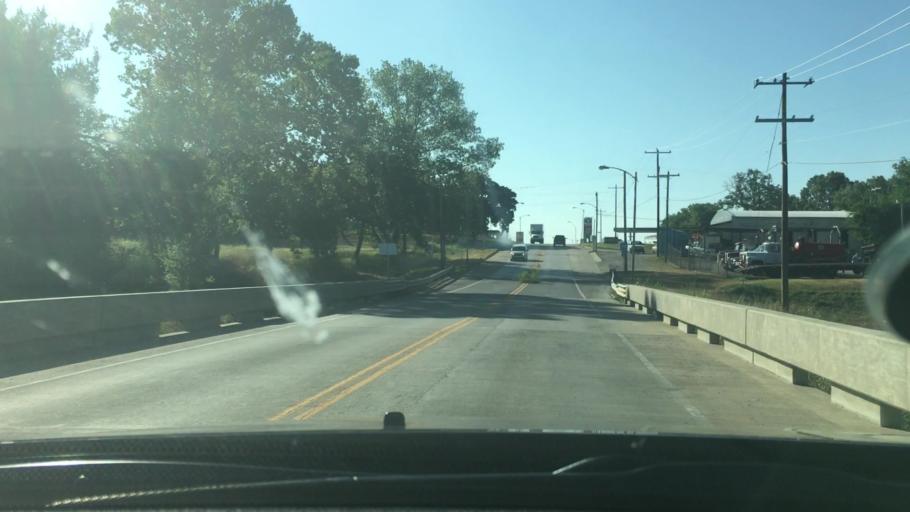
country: US
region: Oklahoma
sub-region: Johnston County
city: Tishomingo
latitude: 34.2391
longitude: -96.6851
